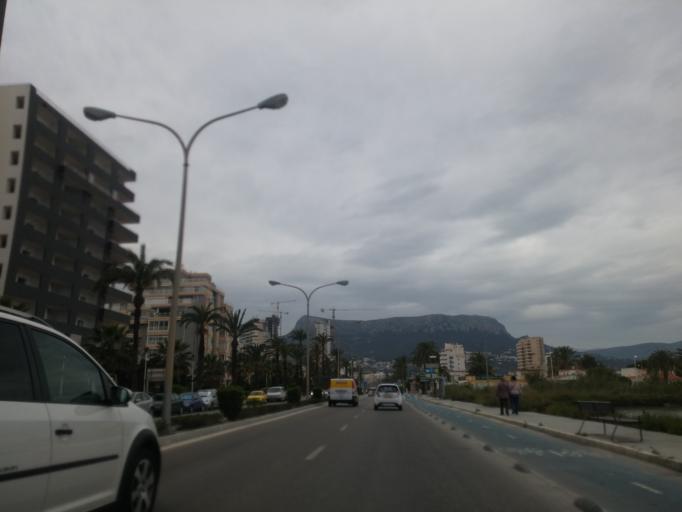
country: ES
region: Valencia
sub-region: Provincia de Alicante
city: Calp
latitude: 38.6425
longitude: 0.0633
